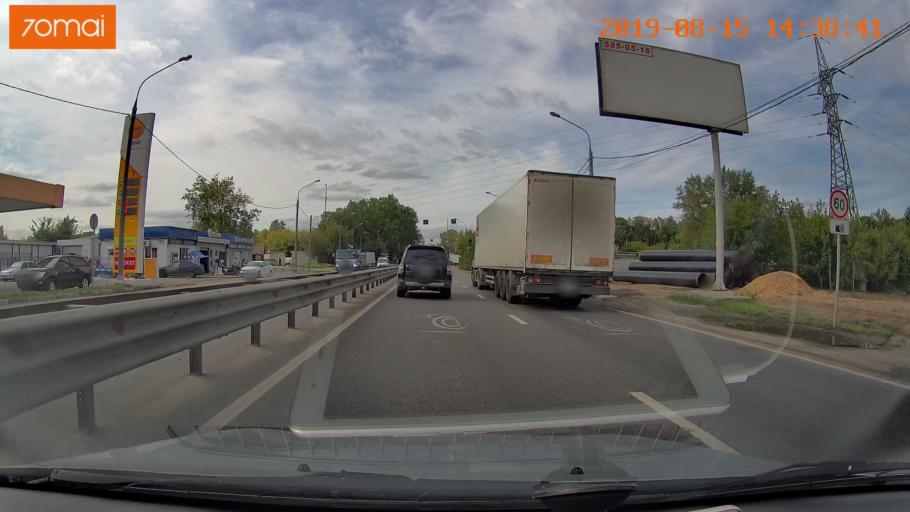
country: RU
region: Moskovskaya
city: Tomilino
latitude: 55.6571
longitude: 37.9194
